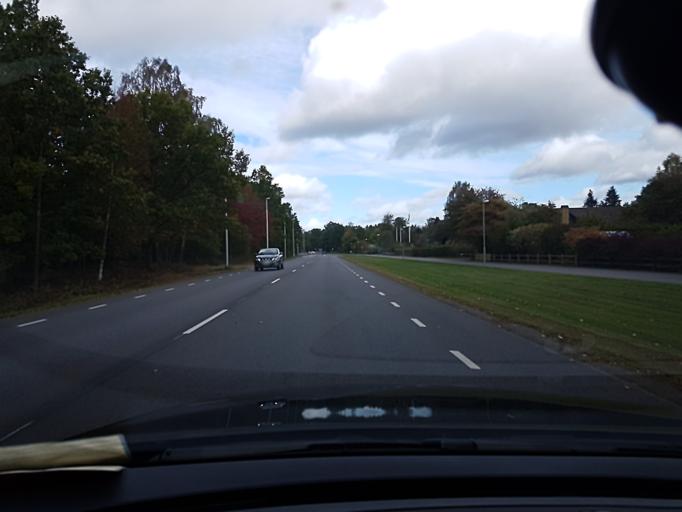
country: SE
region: Kronoberg
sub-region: Vaxjo Kommun
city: Vaexjoe
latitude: 56.8560
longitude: 14.8071
